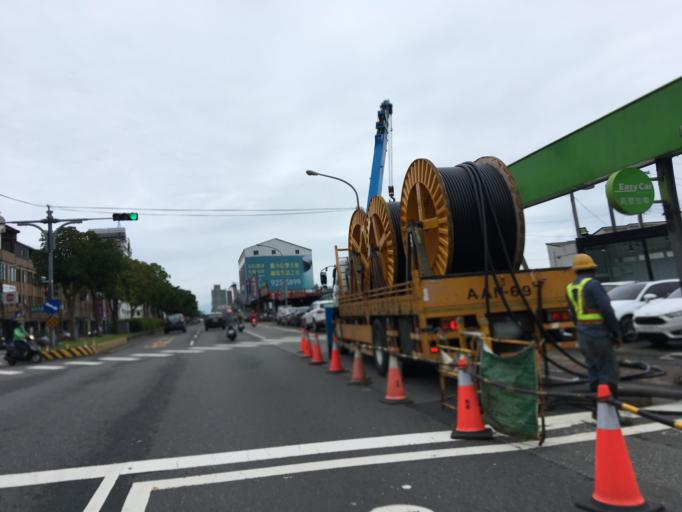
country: TW
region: Taiwan
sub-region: Yilan
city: Yilan
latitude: 24.7008
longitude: 121.7695
